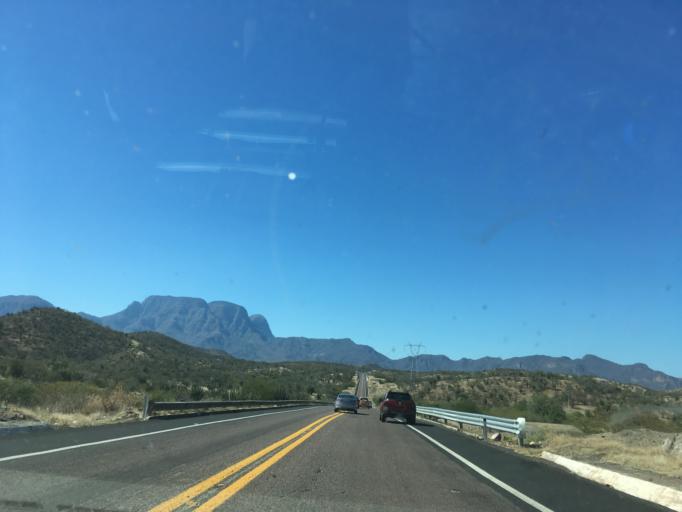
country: MX
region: Michoacan
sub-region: Arteaga
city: Las Canas
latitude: 18.6668
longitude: -101.9864
